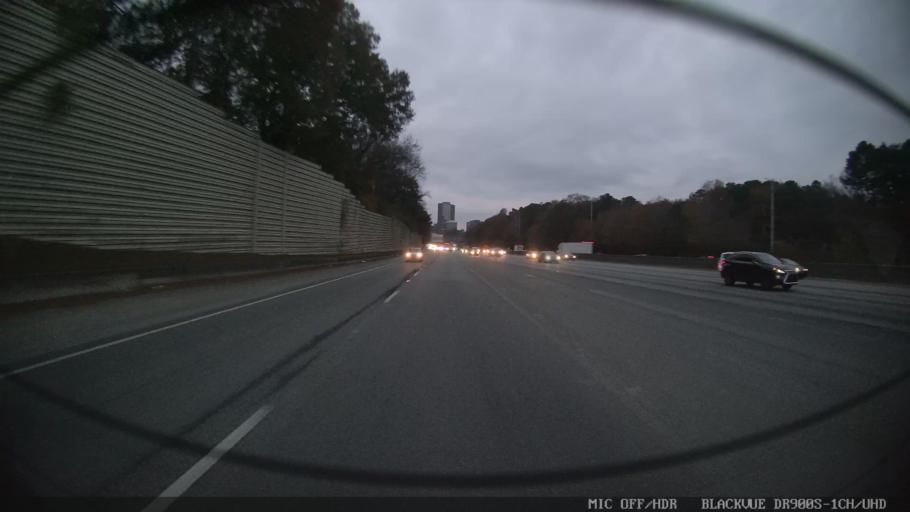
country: US
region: Georgia
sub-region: DeKalb County
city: Dunwoody
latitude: 33.9191
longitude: -84.3182
